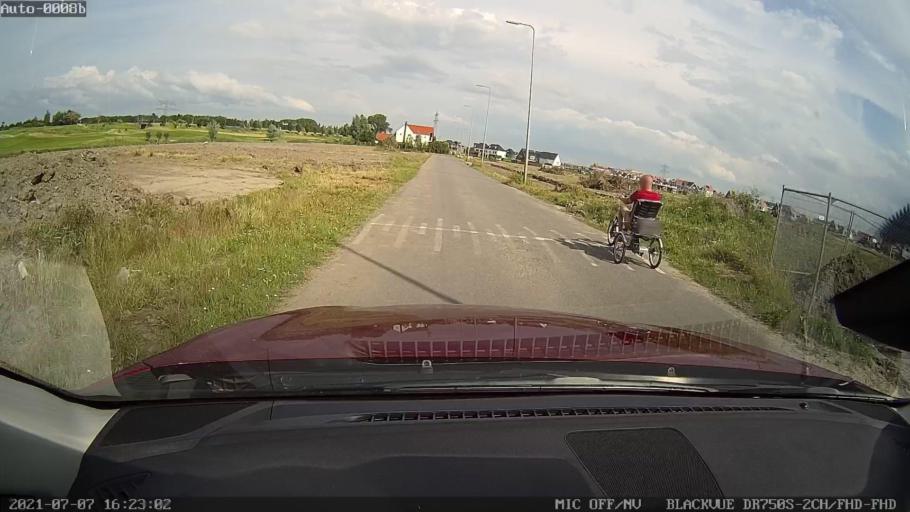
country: NL
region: Zeeland
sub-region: Gemeente Middelburg
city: Middelburg
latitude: 51.4867
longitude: 3.6409
